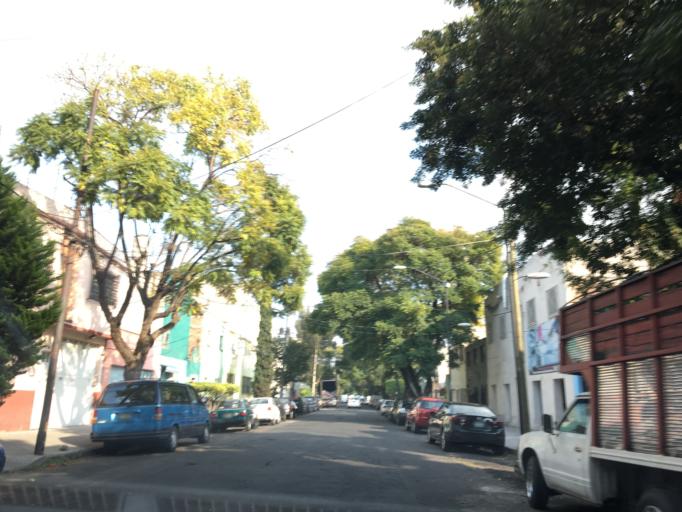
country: MX
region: Mexico City
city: Mexico City
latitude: 19.4175
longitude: -99.1403
